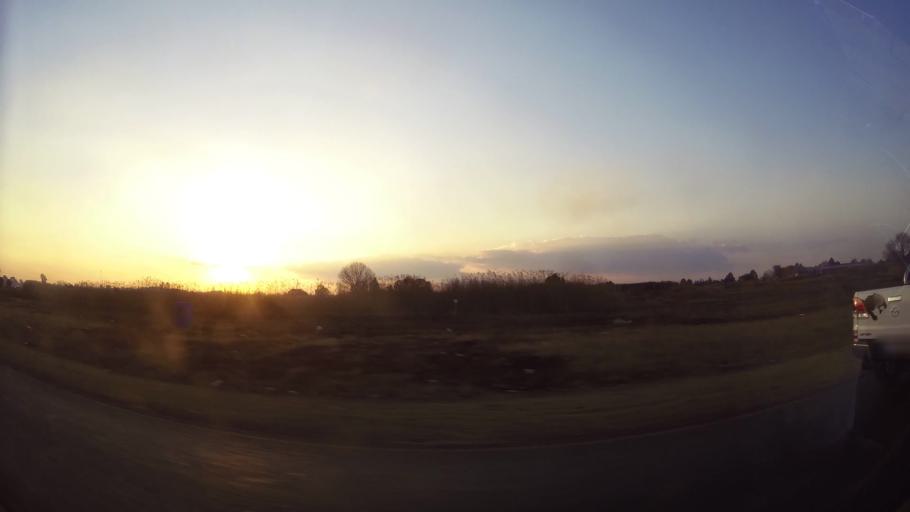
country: ZA
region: Gauteng
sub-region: Ekurhuleni Metropolitan Municipality
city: Springs
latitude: -26.2711
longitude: 28.3987
